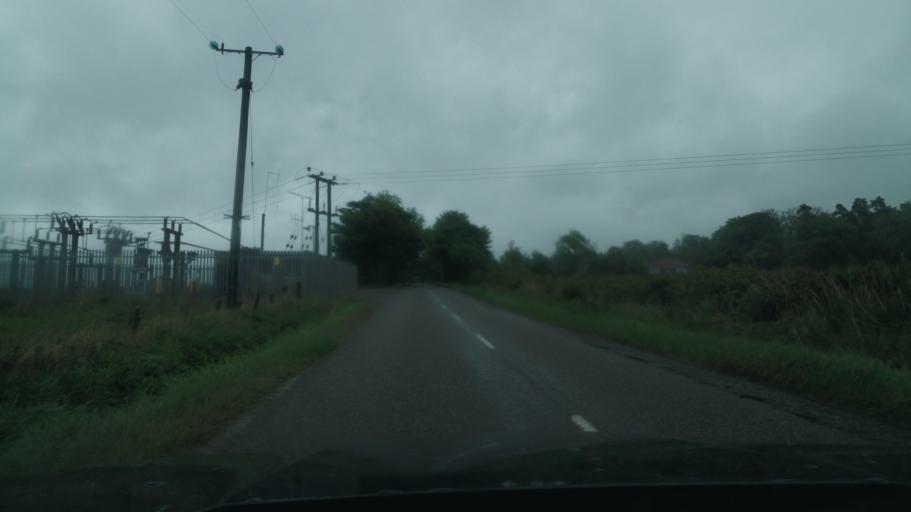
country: GB
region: Scotland
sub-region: Aberdeenshire
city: Huntly
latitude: 57.5438
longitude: -2.8025
